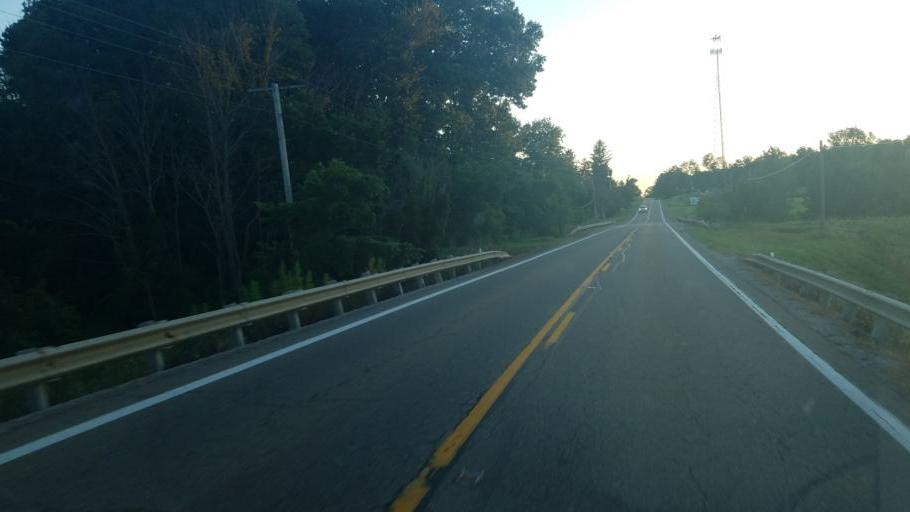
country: US
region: Ohio
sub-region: Morrow County
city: Mount Gilead
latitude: 40.5591
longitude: -82.7613
